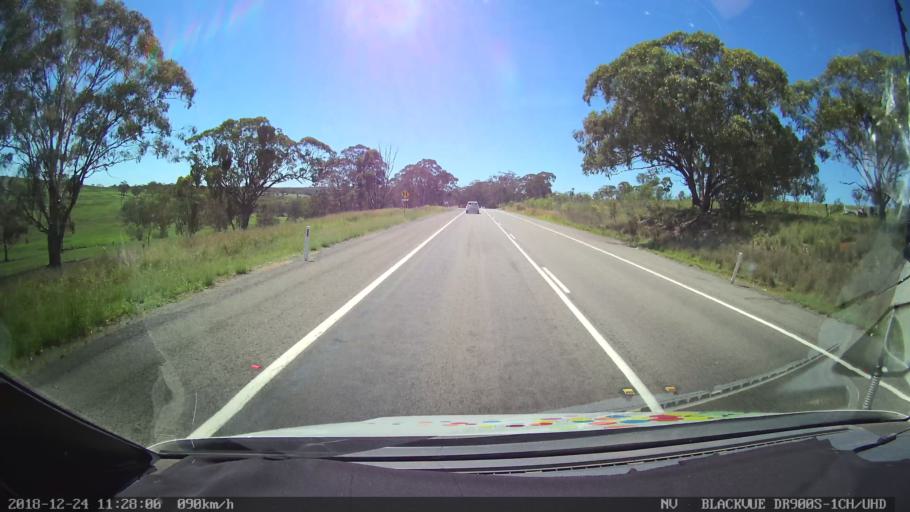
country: AU
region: New South Wales
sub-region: Upper Hunter Shire
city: Merriwa
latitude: -32.1869
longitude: 150.4413
